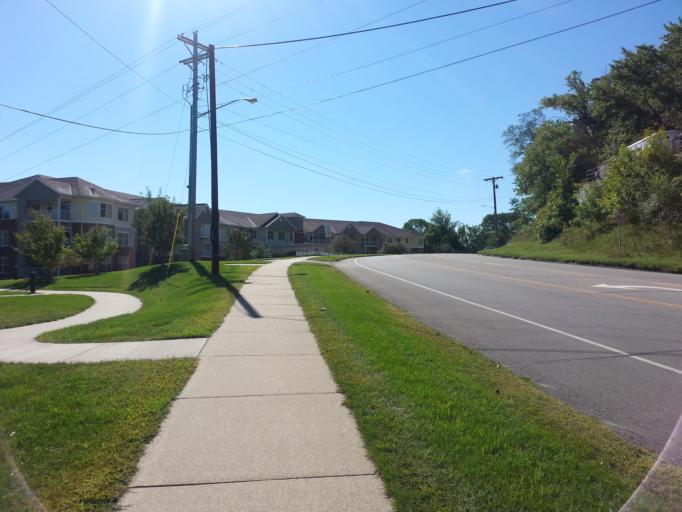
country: US
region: Minnesota
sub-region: Olmsted County
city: Rochester
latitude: 44.0435
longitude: -92.4672
